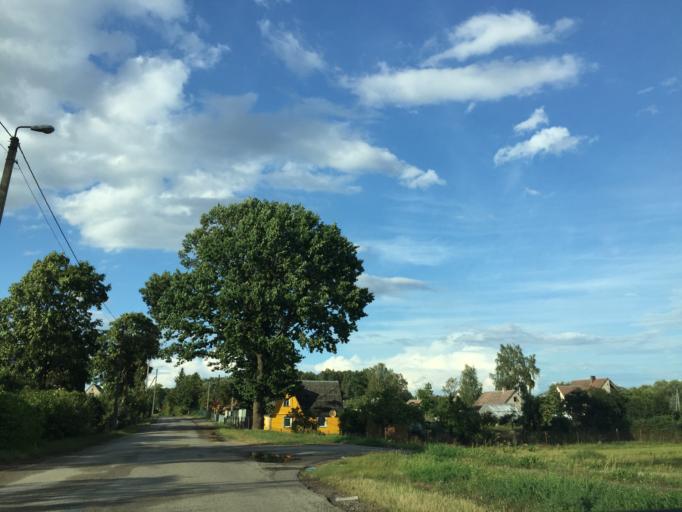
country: LT
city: Zagare
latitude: 56.3667
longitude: 23.2645
